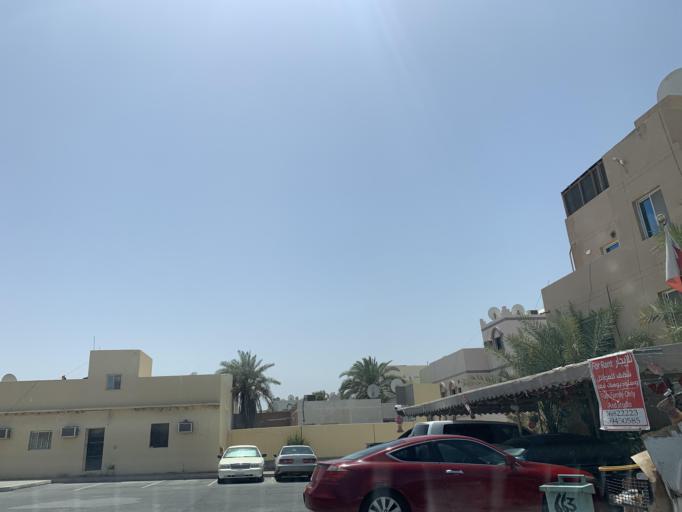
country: BH
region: Northern
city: Ar Rifa'
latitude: 26.1401
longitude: 50.5682
